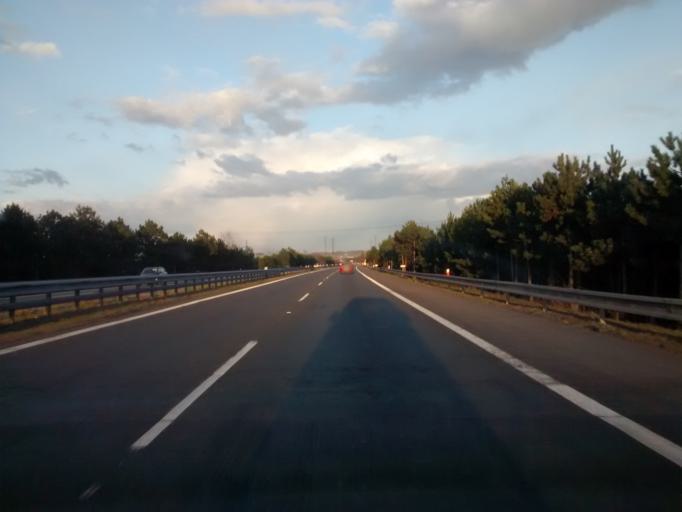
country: CZ
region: Central Bohemia
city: Celakovice
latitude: 50.1334
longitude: 14.7817
